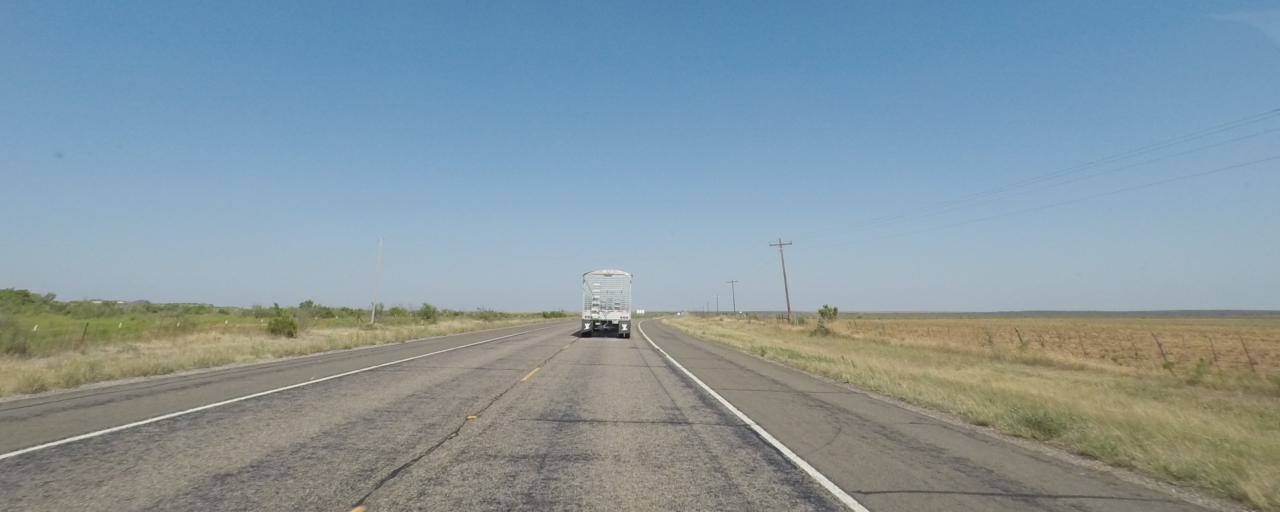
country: US
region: Texas
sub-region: Knox County
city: Benjamin
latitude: 33.5823
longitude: -99.9756
